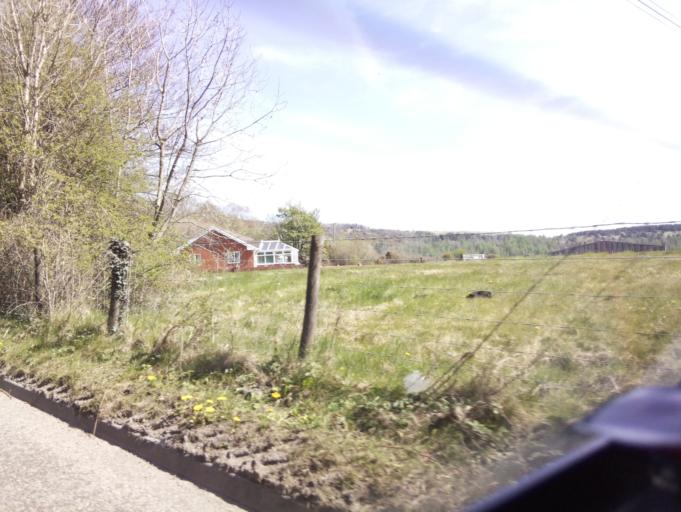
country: GB
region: Wales
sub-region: Rhondda Cynon Taf
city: Aberdare
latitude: 51.7379
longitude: -3.4499
